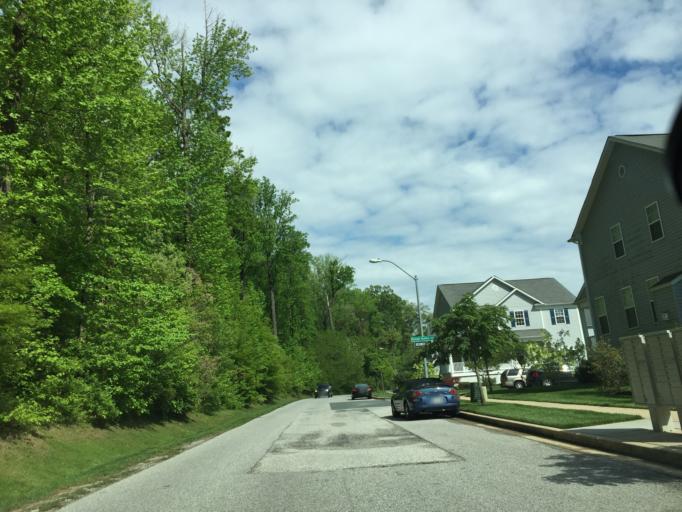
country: US
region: Maryland
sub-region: Baltimore County
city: Middle River
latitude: 39.3174
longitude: -76.4422
